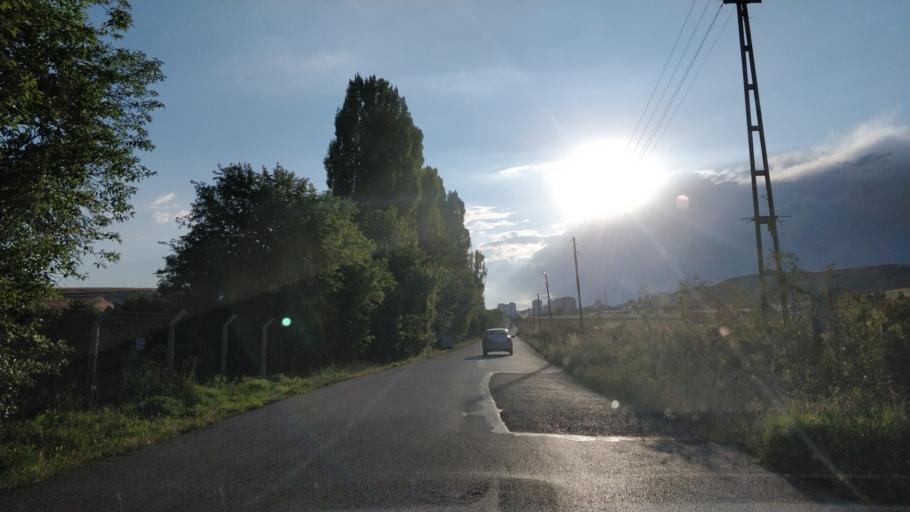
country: TR
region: Ankara
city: Etimesgut
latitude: 39.8260
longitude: 32.5688
